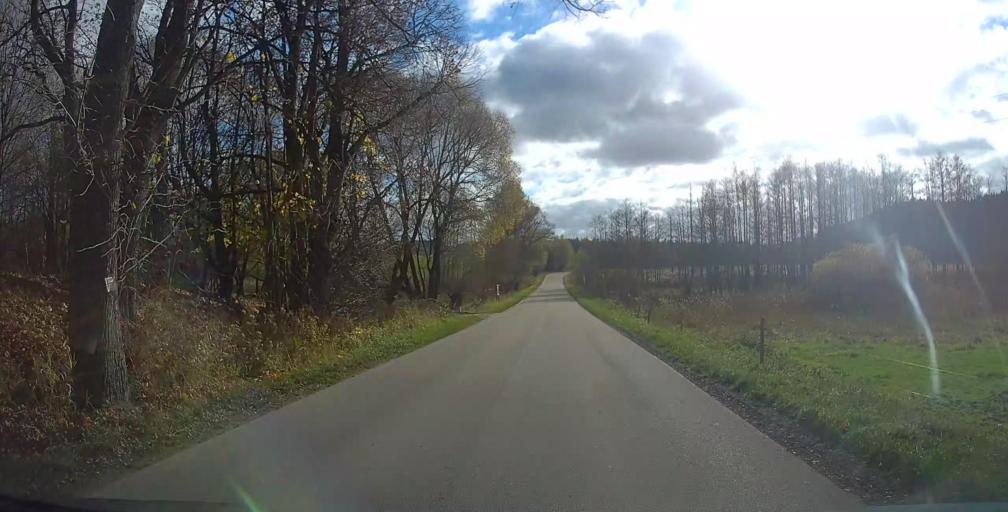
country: PL
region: Podlasie
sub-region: Suwalki
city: Suwalki
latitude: 54.2797
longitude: 22.9088
